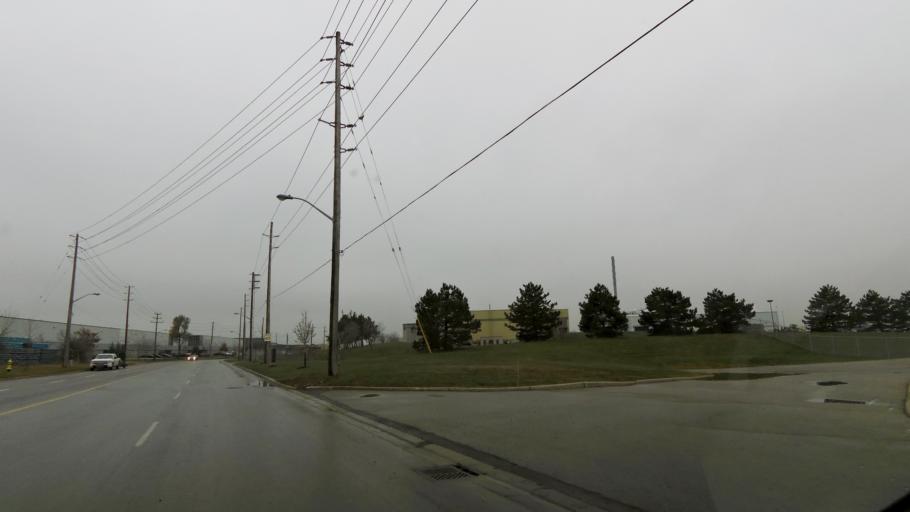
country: CA
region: Ontario
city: Etobicoke
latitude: 43.7029
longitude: -79.6027
